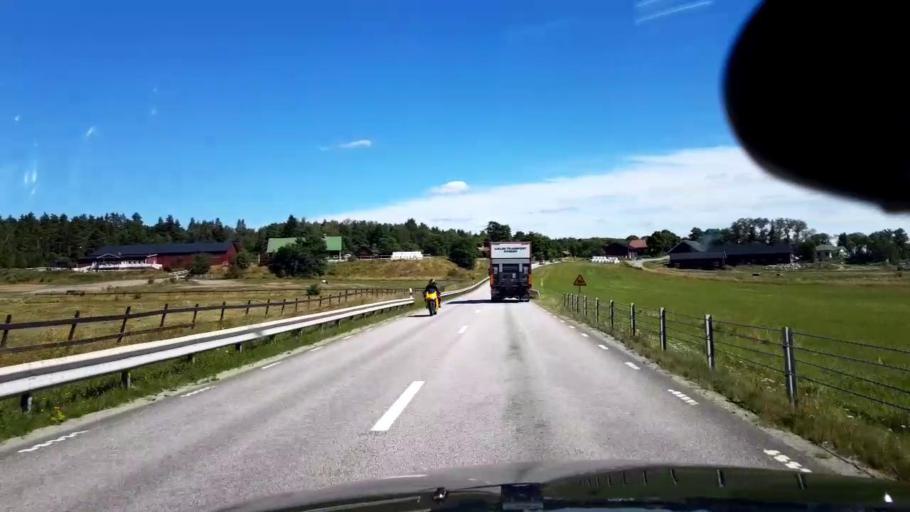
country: SE
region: Stockholm
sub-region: Sigtuna Kommun
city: Sigtuna
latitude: 59.6571
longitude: 17.6731
